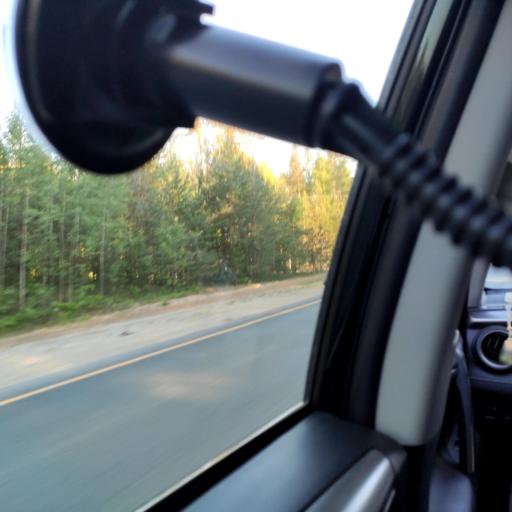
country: RU
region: Mariy-El
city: Suslonger
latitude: 56.2516
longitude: 48.2321
